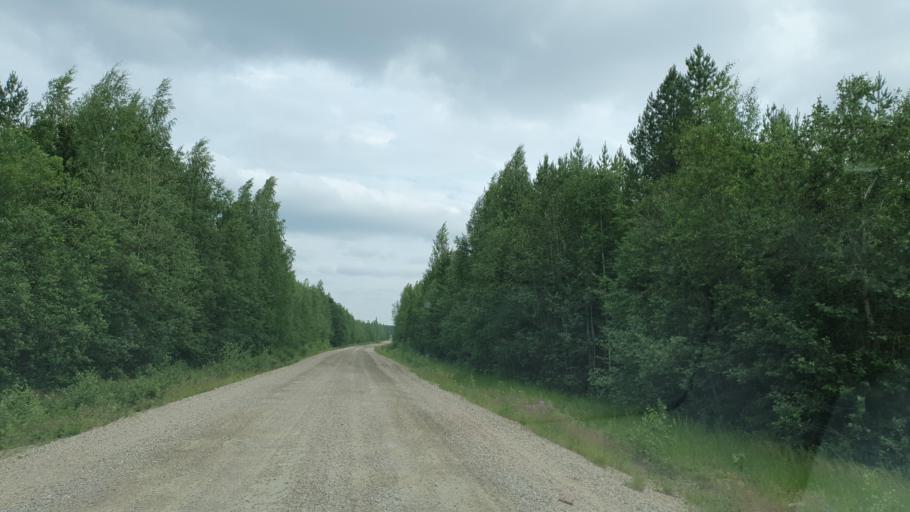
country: FI
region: Kainuu
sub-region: Kehys-Kainuu
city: Kuhmo
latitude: 63.9448
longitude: 29.4060
